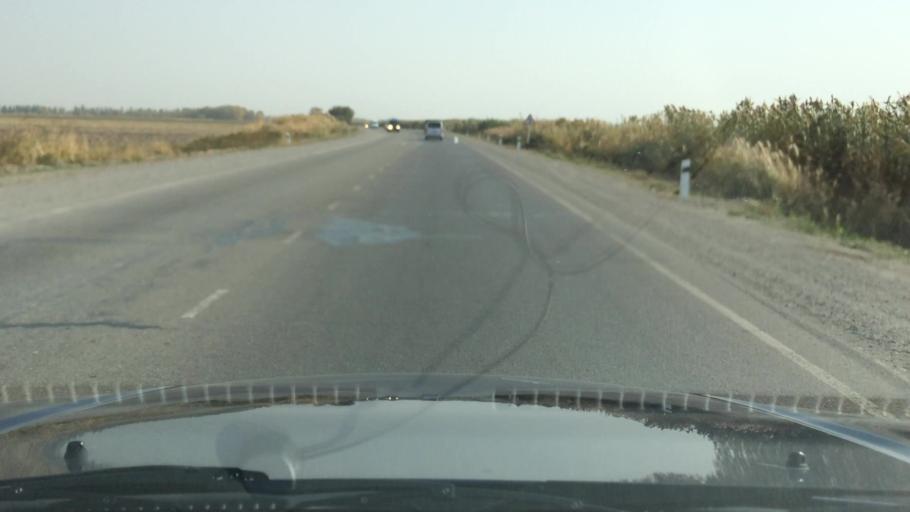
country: KG
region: Chuy
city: Lebedinovka
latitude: 42.9194
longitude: 74.7187
